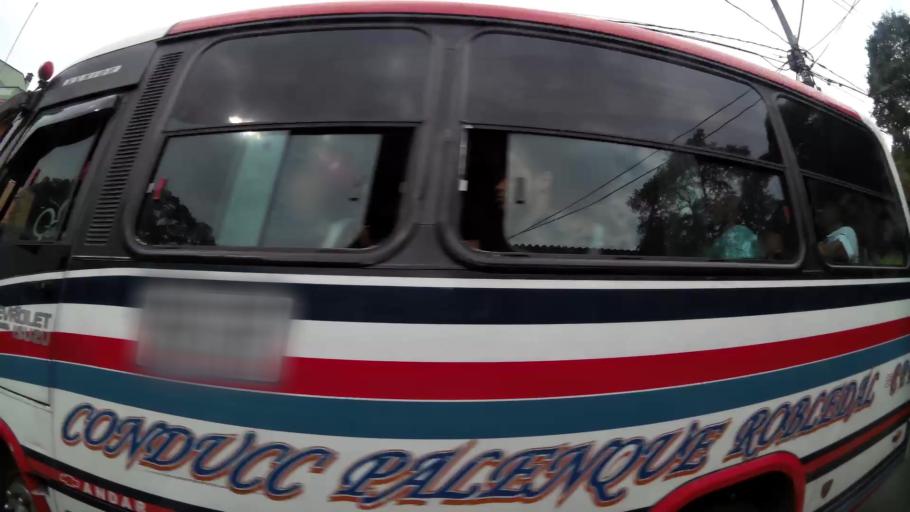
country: CO
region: Antioquia
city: Medellin
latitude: 6.2801
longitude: -75.5939
